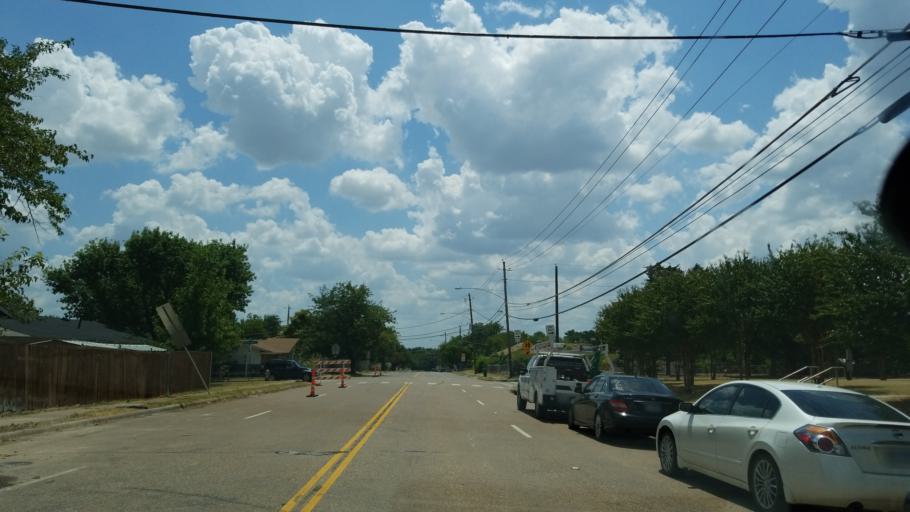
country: US
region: Texas
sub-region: Dallas County
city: Cockrell Hill
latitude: 32.7153
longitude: -96.9001
